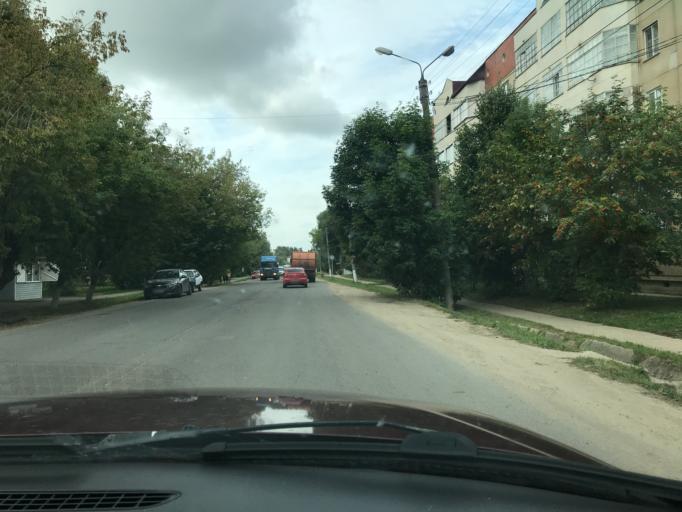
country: RU
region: Kaluga
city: Maloyaroslavets
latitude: 55.0081
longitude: 36.4728
